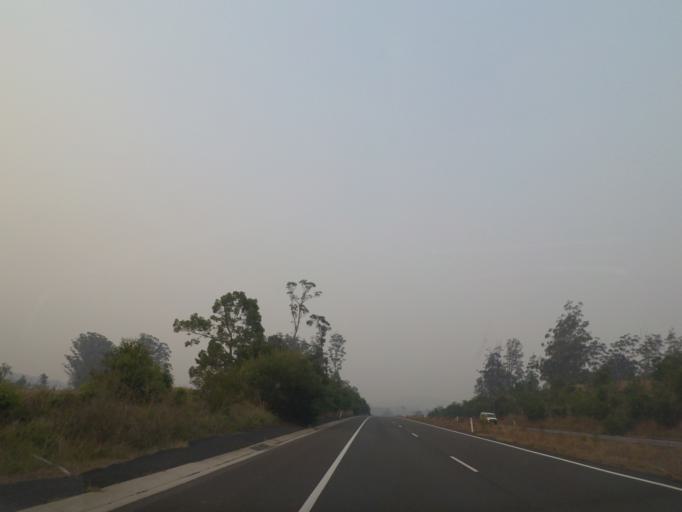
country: AU
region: New South Wales
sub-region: Nambucca Shire
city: Macksville
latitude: -30.7741
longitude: 152.8973
